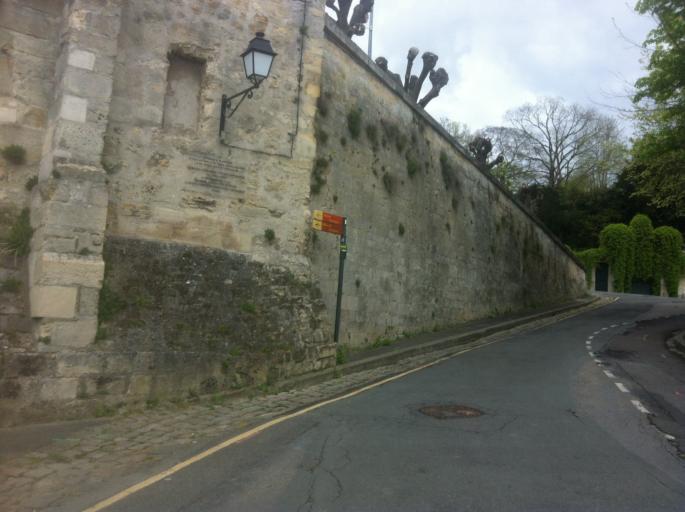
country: FR
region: Ile-de-France
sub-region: Departement du Val-d'Oise
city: Auvers-sur-Oise
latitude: 49.0717
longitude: 2.1767
